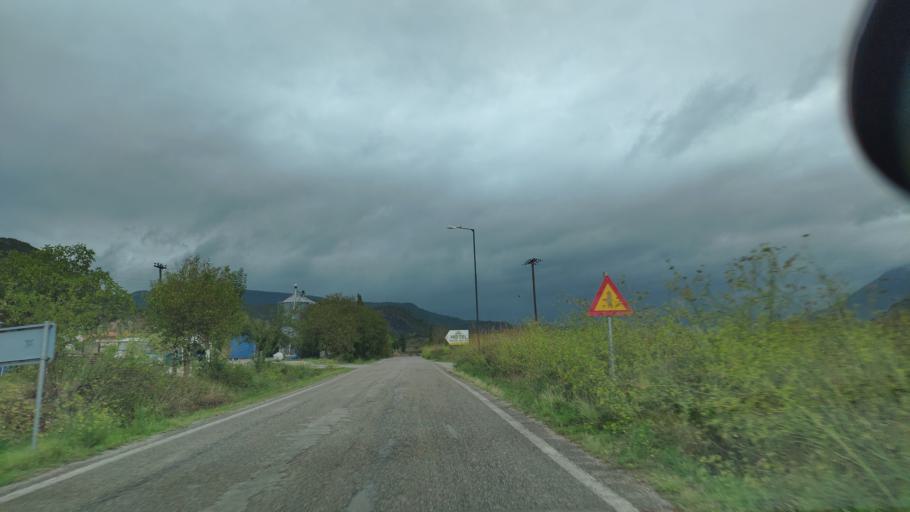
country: GR
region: West Greece
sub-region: Nomos Aitolias kai Akarnanias
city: Krikellos
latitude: 38.9771
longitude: 21.3264
